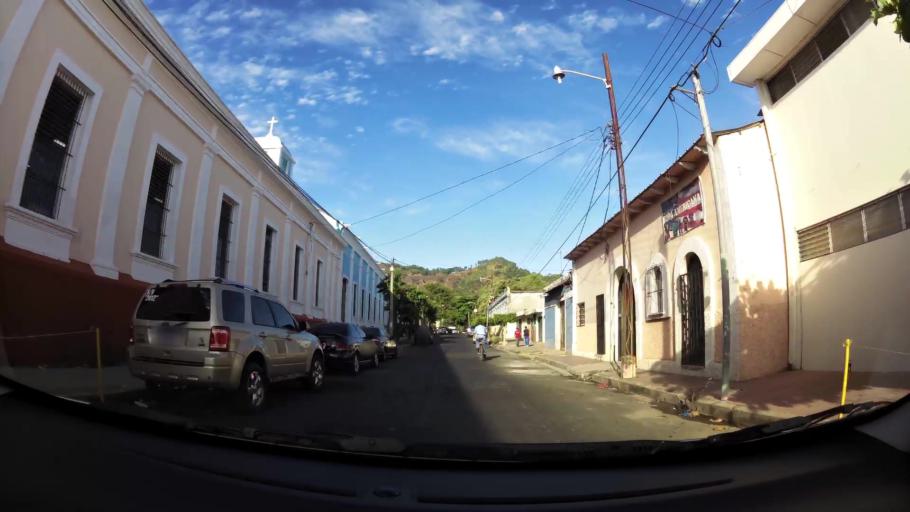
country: SV
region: Santa Ana
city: Santa Ana
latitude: 13.9983
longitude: -89.5616
